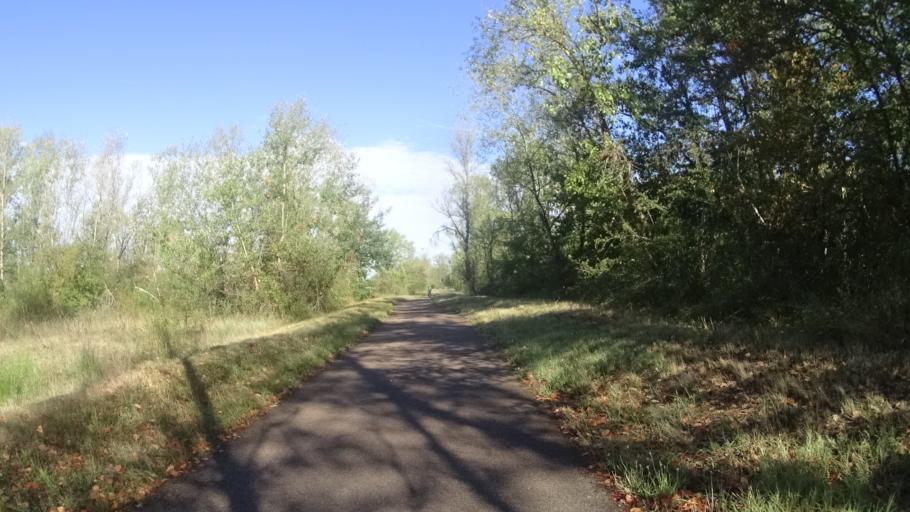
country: FR
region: Bourgogne
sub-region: Departement de la Nievre
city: Pouilly-sur-Loire
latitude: 47.3021
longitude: 2.9163
